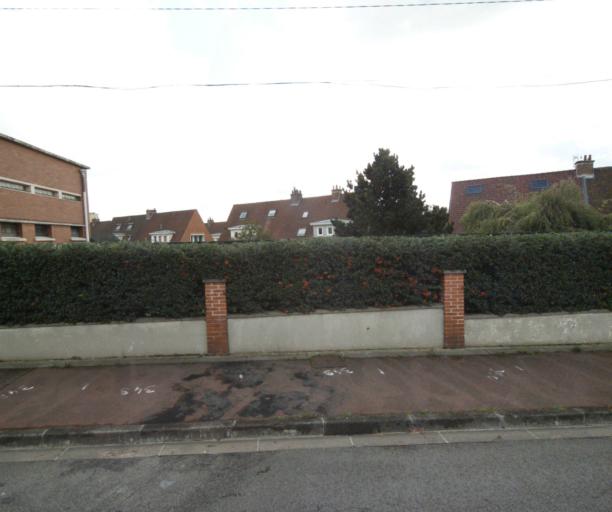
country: FR
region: Nord-Pas-de-Calais
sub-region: Departement du Nord
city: Lomme
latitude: 50.6441
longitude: 2.9854
